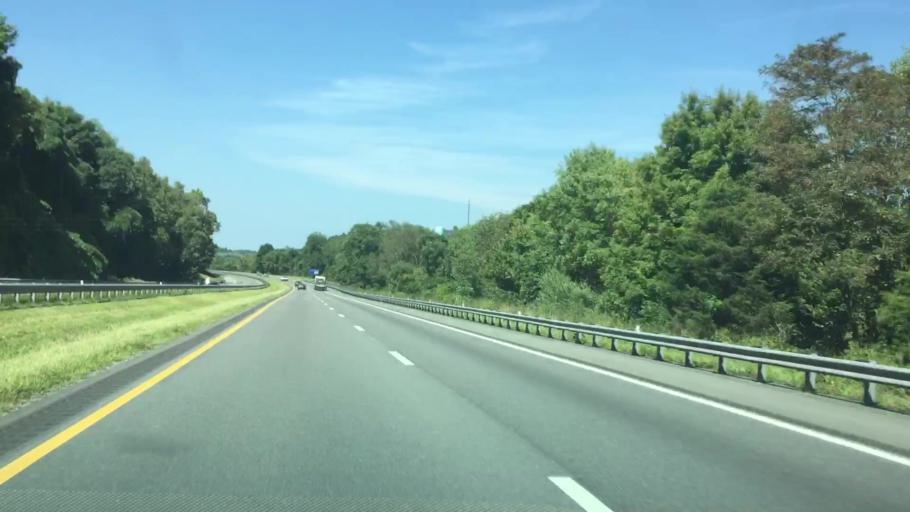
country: US
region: Virginia
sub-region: Smyth County
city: Chilhowie
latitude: 36.8086
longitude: -81.6521
